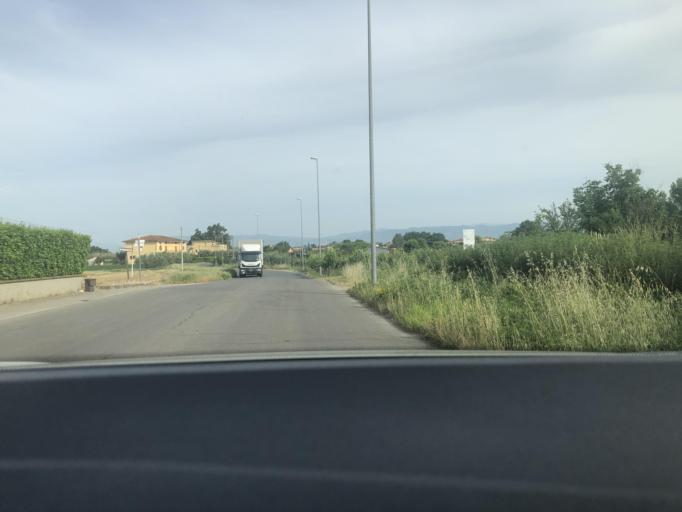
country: IT
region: Tuscany
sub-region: Provincia di Pistoia
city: San Rocco
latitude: 43.8128
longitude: 10.8637
